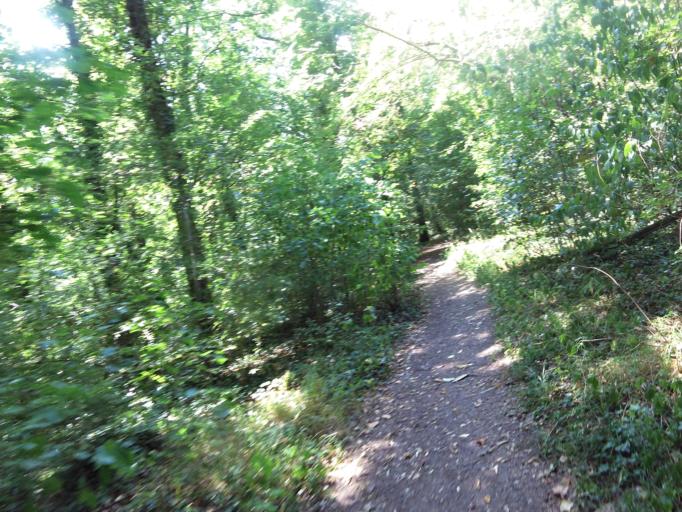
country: DE
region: Bavaria
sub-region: Regierungsbezirk Unterfranken
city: Randersacker
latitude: 49.7409
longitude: 9.9530
